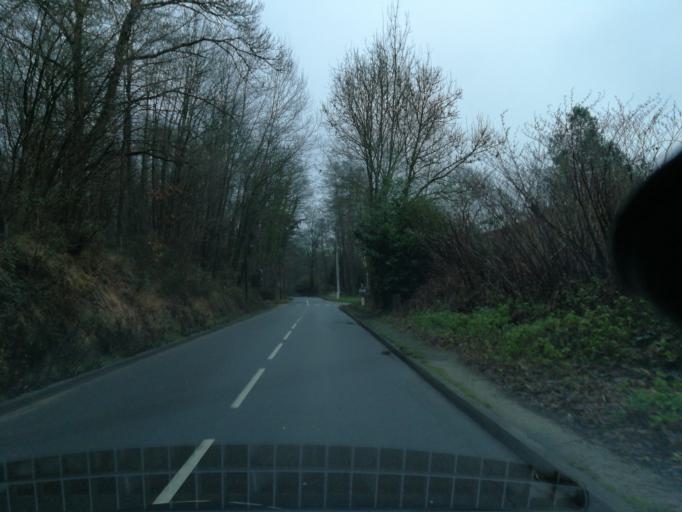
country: FR
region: Ile-de-France
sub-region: Departement des Yvelines
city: Les Loges-en-Josas
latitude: 48.7724
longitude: 2.1408
